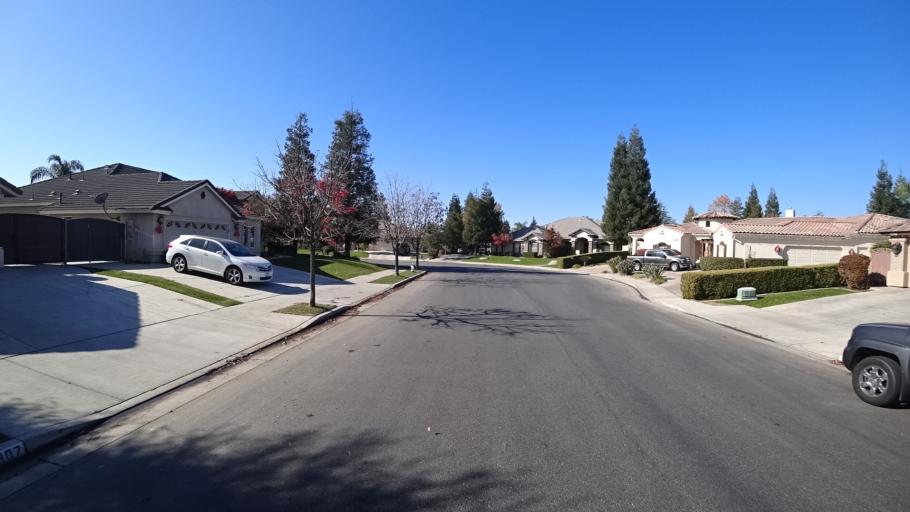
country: US
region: California
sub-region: Kern County
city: Rosedale
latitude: 35.3660
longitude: -119.1391
